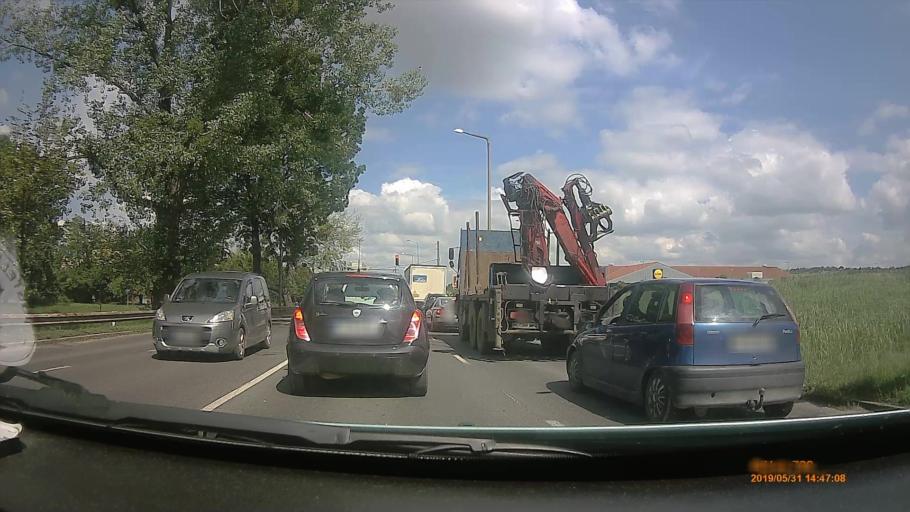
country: HU
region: Borsod-Abauj-Zemplen
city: Miskolc
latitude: 48.1003
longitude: 20.7446
